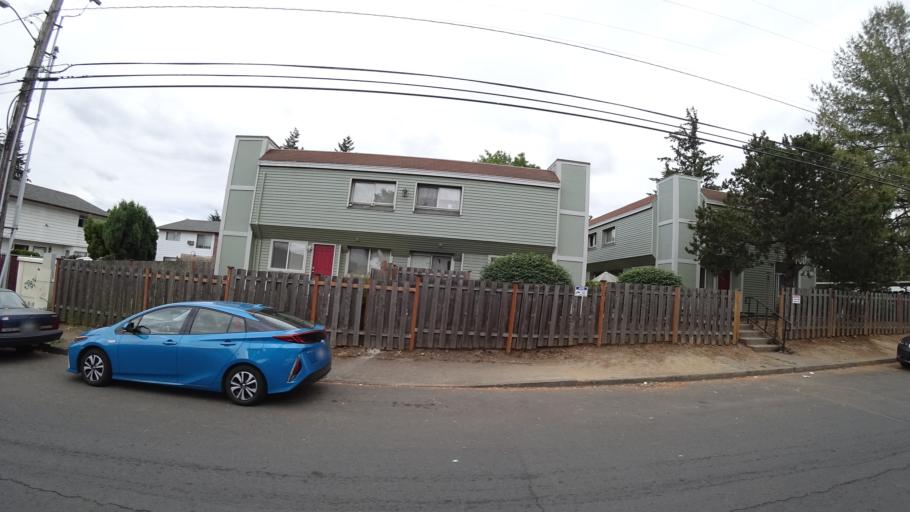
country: US
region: Oregon
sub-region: Multnomah County
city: Lents
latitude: 45.5033
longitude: -122.5409
